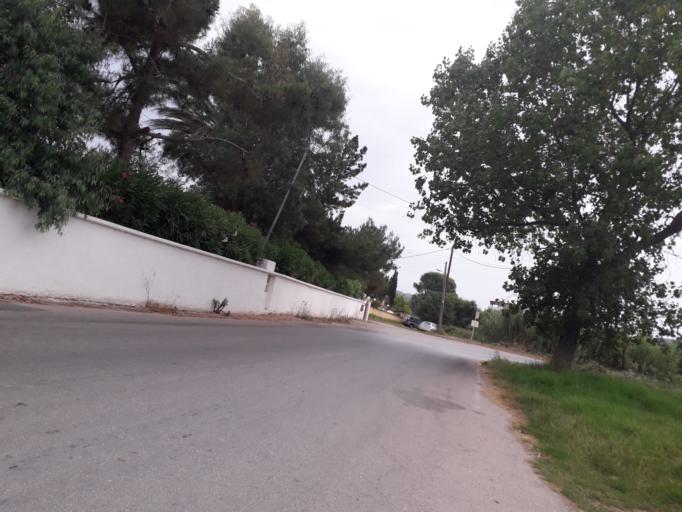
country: GR
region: Ionian Islands
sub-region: Nomos Kerkyras
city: Perivoli
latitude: 39.4296
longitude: 19.9503
